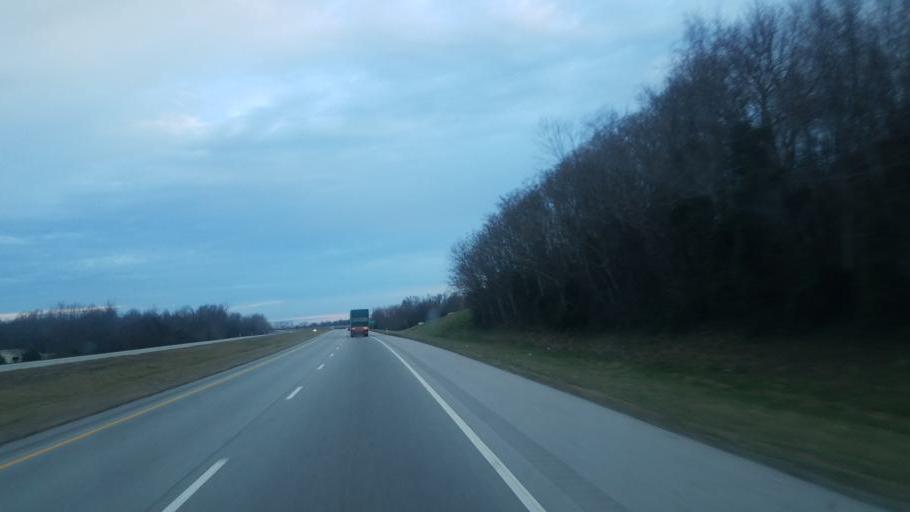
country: US
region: Tennessee
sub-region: White County
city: Sparta
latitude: 36.0086
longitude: -85.5047
